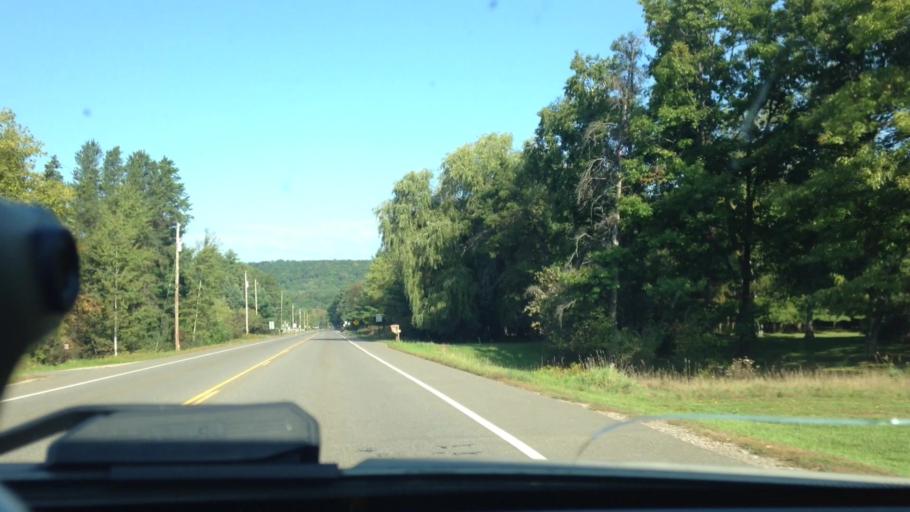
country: US
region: Michigan
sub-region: Dickinson County
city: Quinnesec
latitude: 45.8374
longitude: -88.0105
